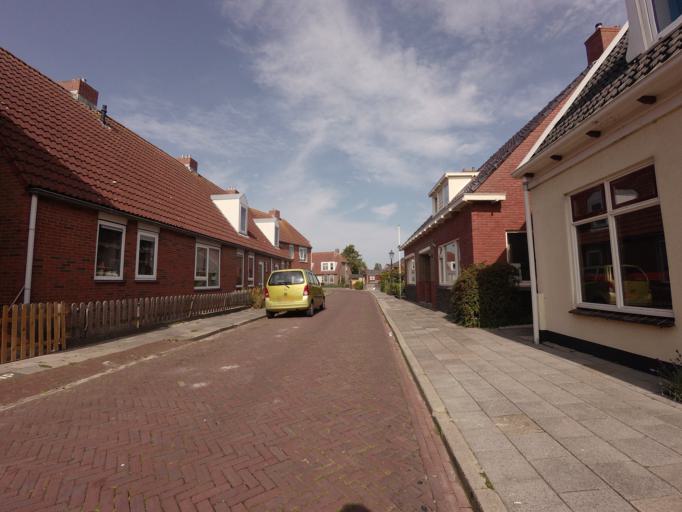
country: NL
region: Groningen
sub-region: Gemeente De Marne
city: Ulrum
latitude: 53.3376
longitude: 6.3009
